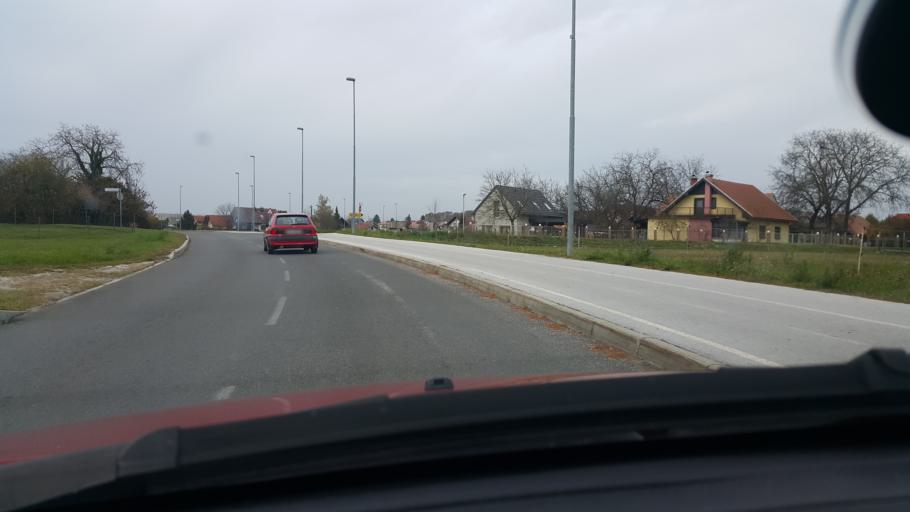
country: HR
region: Zagrebacka
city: Bregana
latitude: 45.8973
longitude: 15.6619
